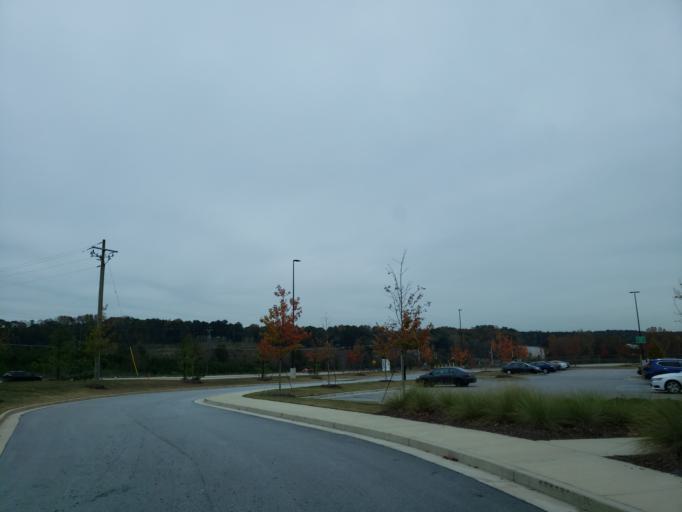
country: US
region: Georgia
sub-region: Cobb County
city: Mableton
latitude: 33.7855
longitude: -84.5058
